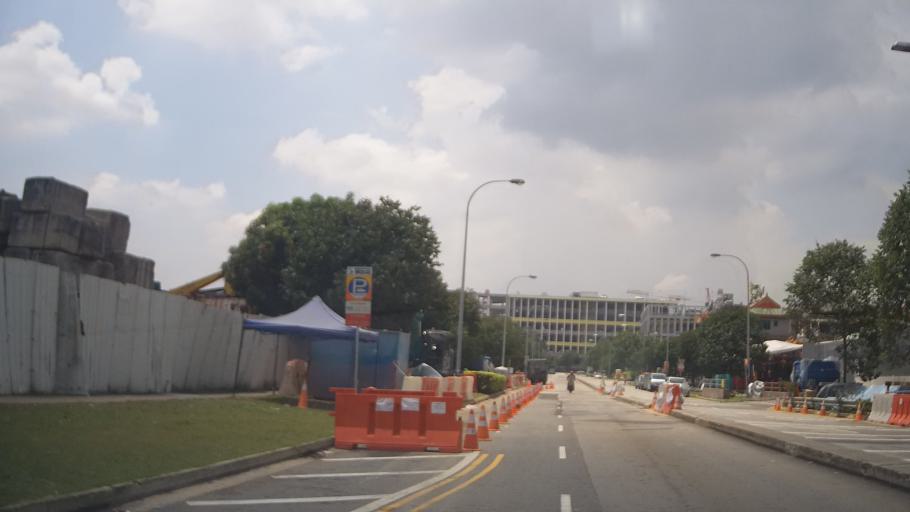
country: MY
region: Johor
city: Johor Bahru
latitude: 1.4512
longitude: 103.8008
